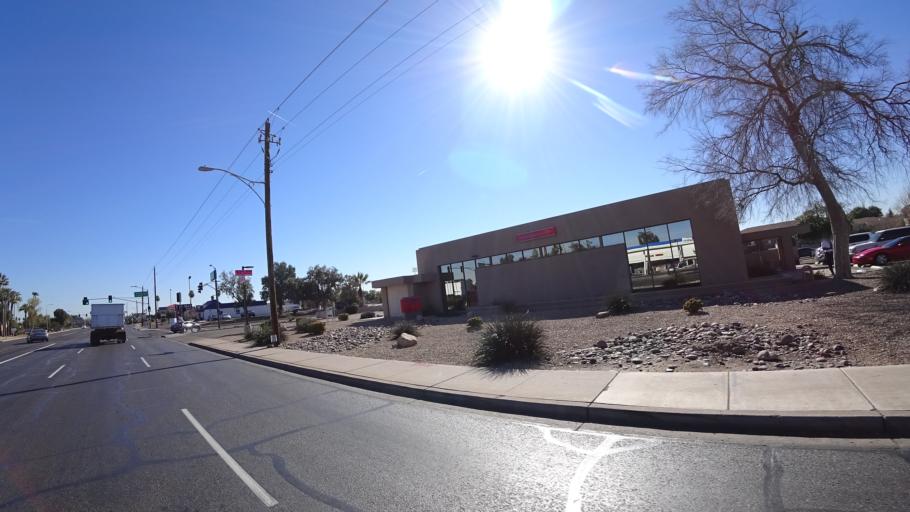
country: US
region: Arizona
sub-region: Maricopa County
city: Glendale
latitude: 33.4949
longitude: -112.1760
